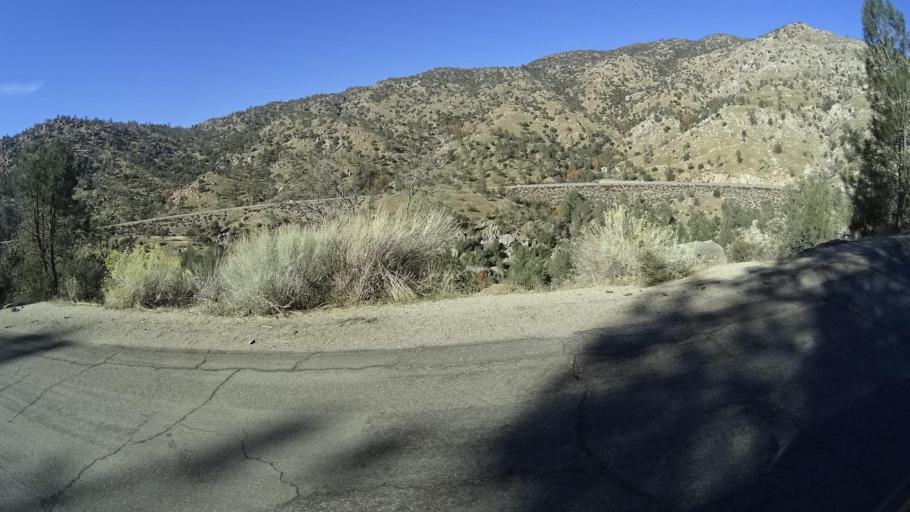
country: US
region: California
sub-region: Kern County
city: Bodfish
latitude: 35.5650
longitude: -118.5801
